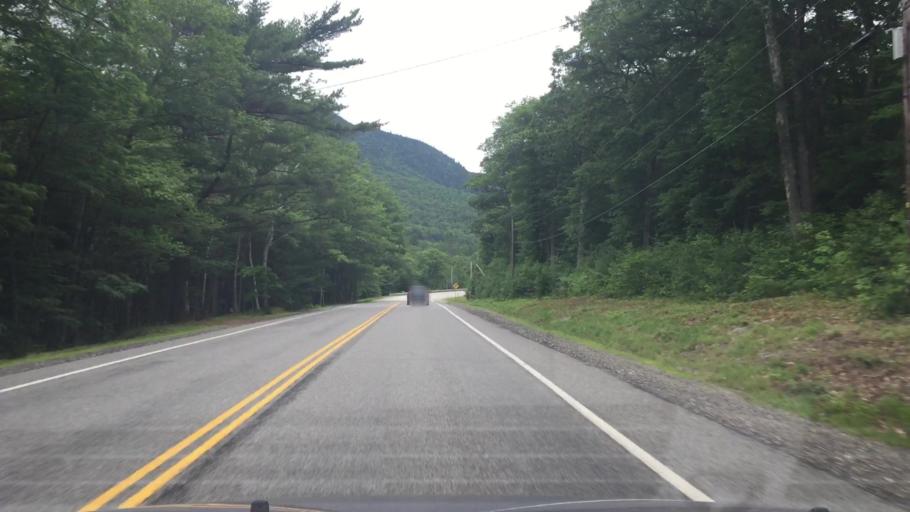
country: US
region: New Hampshire
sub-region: Carroll County
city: North Conway
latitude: 44.1235
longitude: -71.3565
